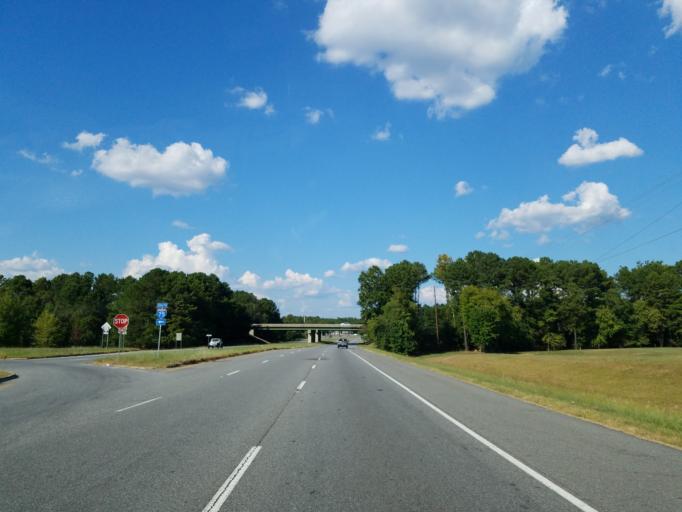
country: US
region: Georgia
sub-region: Bartow County
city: Cartersville
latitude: 34.2435
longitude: -84.7743
